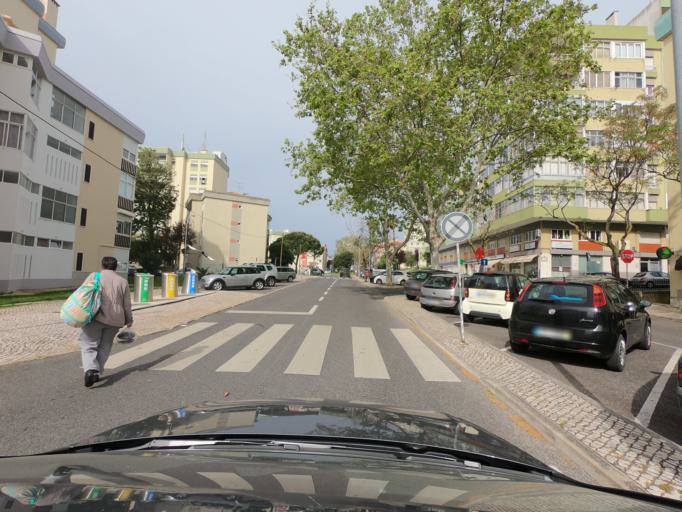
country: PT
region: Lisbon
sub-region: Oeiras
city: Oeiras
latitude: 38.6944
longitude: -9.3035
